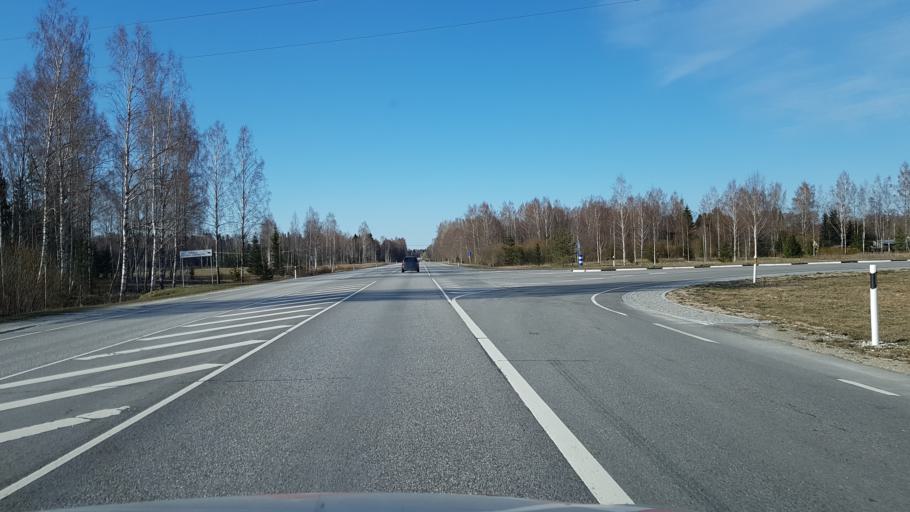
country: EE
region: Ida-Virumaa
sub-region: Johvi vald
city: Johvi
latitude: 59.1886
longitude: 27.3470
